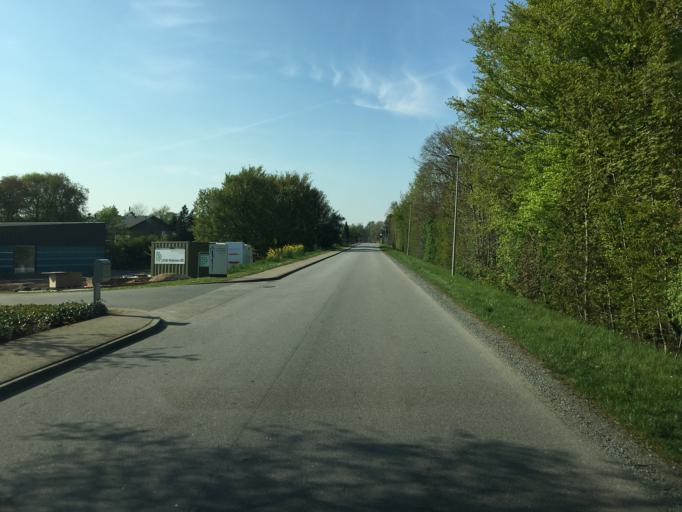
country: DK
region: South Denmark
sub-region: Haderslev Kommune
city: Vojens
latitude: 55.2447
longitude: 9.3170
